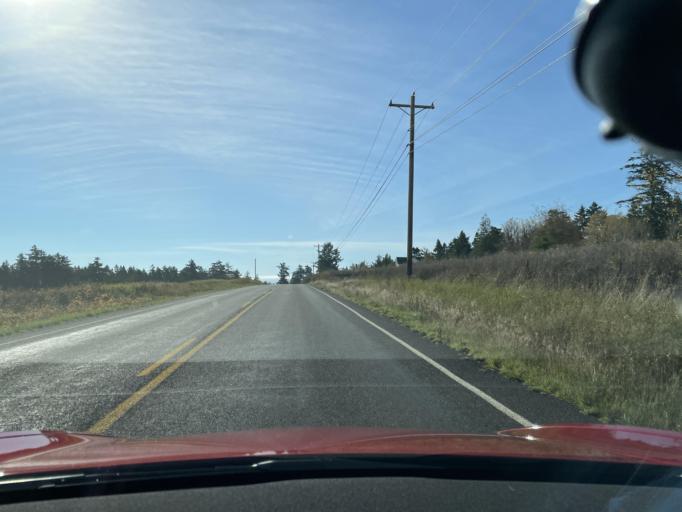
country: US
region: Washington
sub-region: San Juan County
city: Friday Harbor
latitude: 48.4749
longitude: -123.0329
